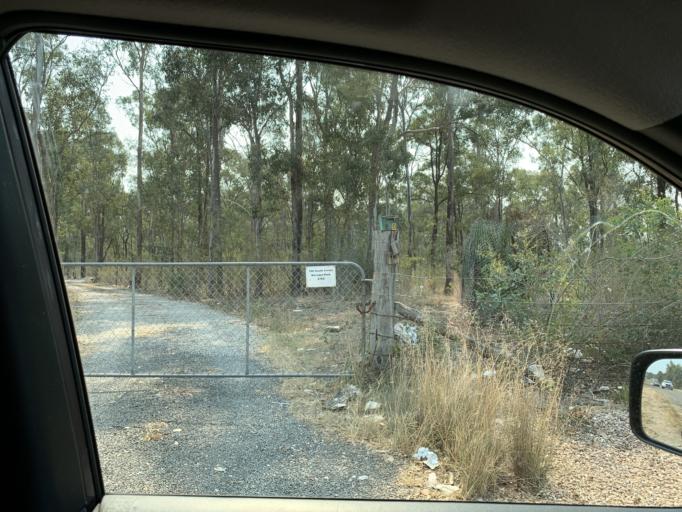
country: AU
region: New South Wales
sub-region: Blacktown
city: Blackett
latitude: -33.7144
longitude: 150.8205
